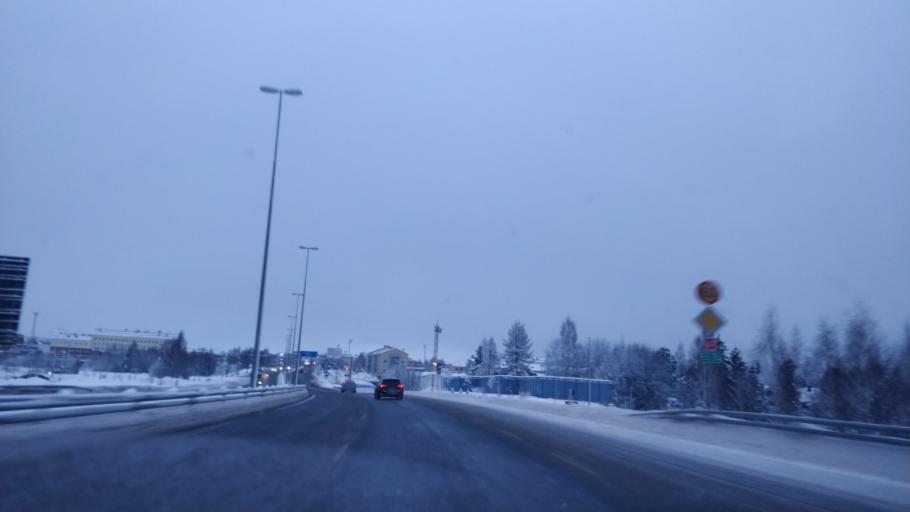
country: FI
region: Lapland
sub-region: Rovaniemi
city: Rovaniemi
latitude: 66.4929
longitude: 25.7091
